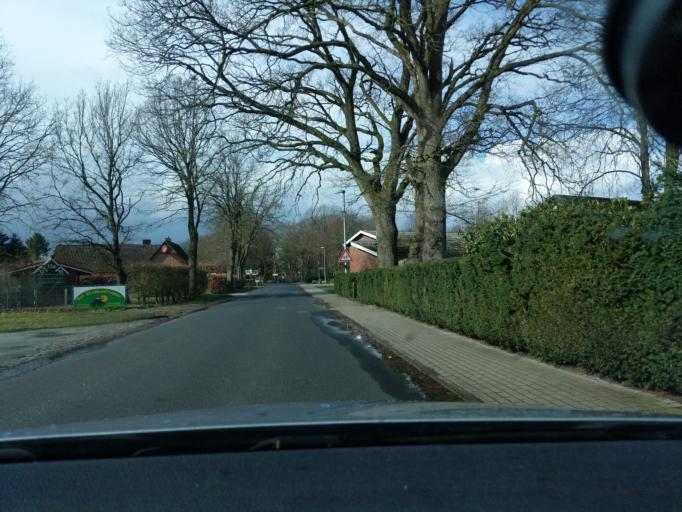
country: DE
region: Lower Saxony
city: Kranenburg
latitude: 53.6048
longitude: 9.2081
